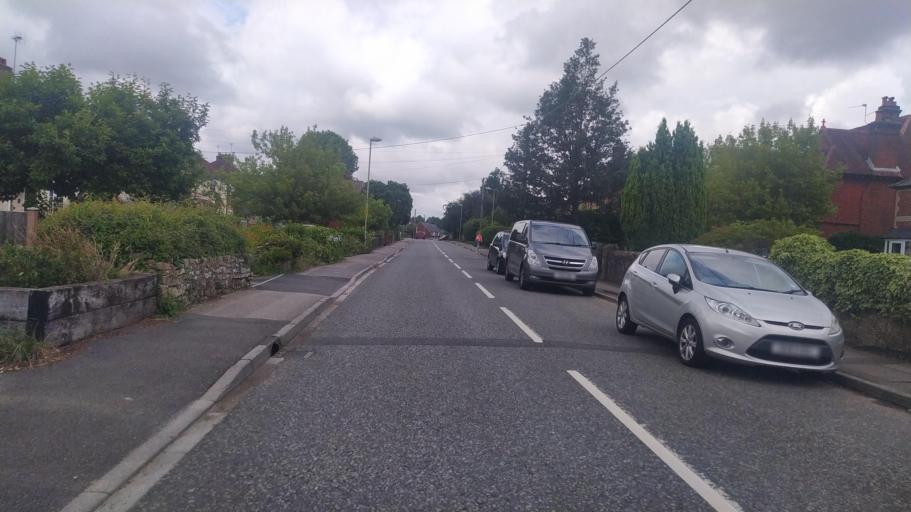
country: GB
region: England
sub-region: Hampshire
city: Liphook
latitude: 51.0789
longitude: -0.8042
